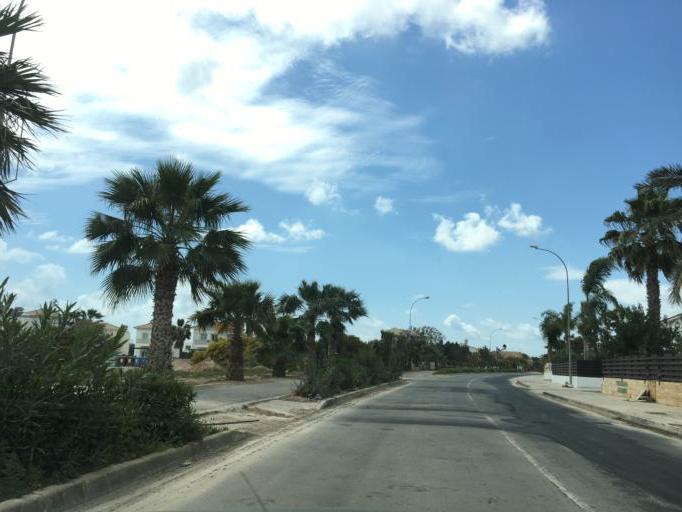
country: CY
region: Ammochostos
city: Liopetri
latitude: 34.9758
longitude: 33.9085
